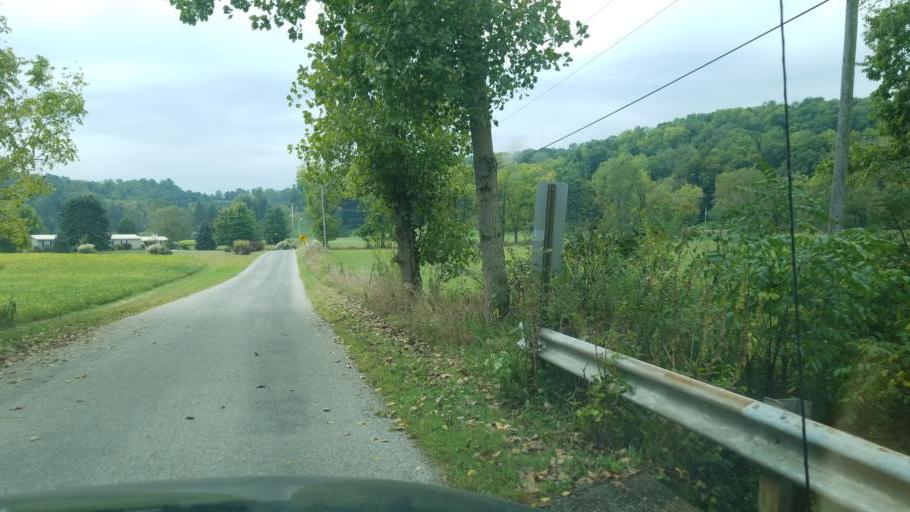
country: US
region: Ohio
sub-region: Licking County
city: Granville
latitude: 40.1174
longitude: -82.4616
